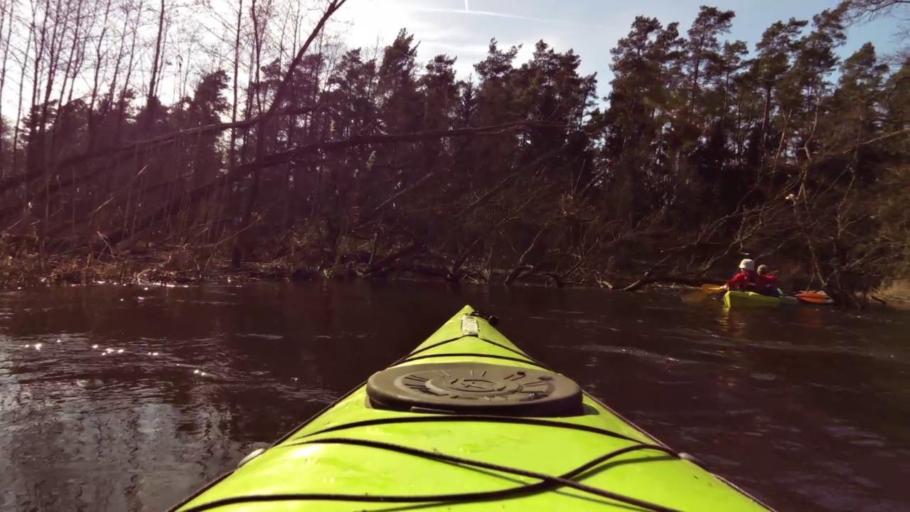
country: PL
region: West Pomeranian Voivodeship
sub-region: Powiat lobeski
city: Lobez
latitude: 53.6853
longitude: 15.5621
